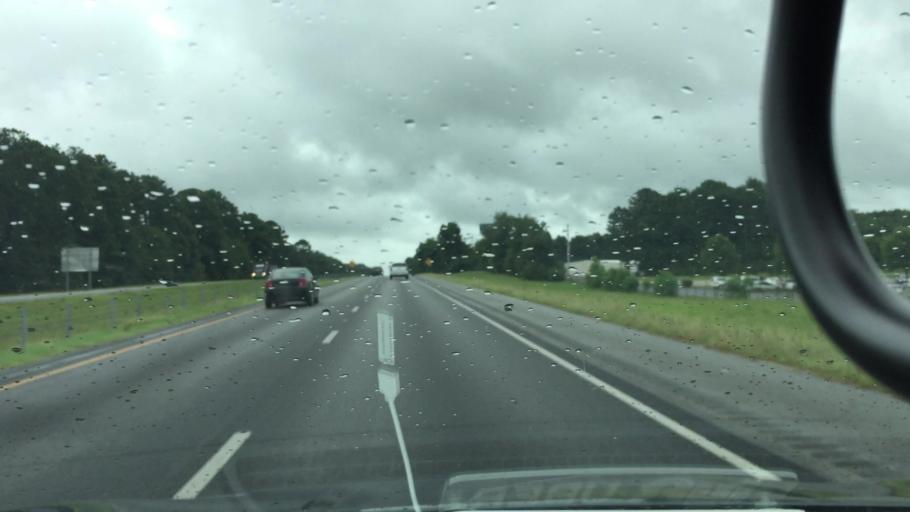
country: US
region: Alabama
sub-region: Lee County
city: Opelika
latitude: 32.6212
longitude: -85.3926
